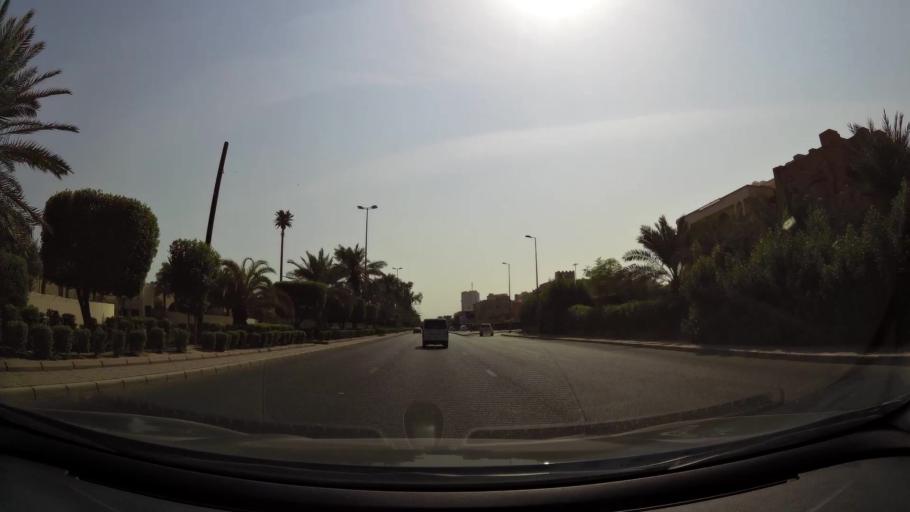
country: KW
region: Al Ahmadi
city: Al Manqaf
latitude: 29.1093
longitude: 48.1366
